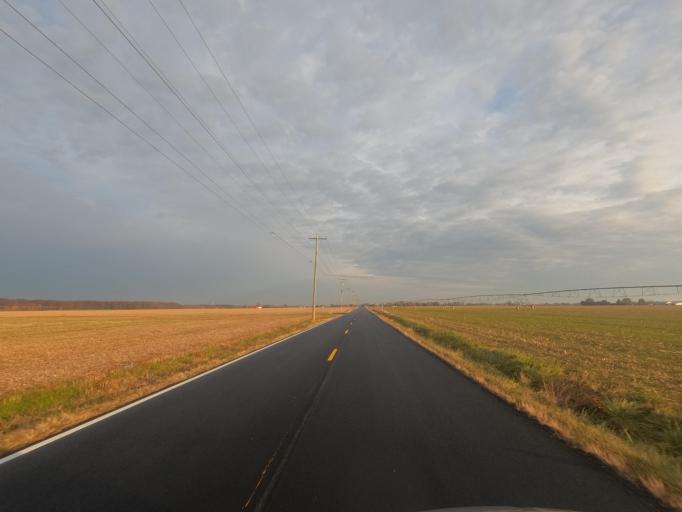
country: US
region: Delaware
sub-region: New Castle County
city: Townsend
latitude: 39.2956
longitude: -75.8309
